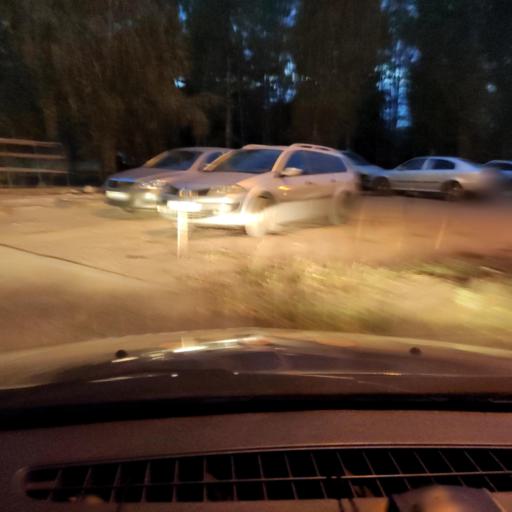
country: RU
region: Voronezj
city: Pridonskoy
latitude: 51.6735
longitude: 39.1028
